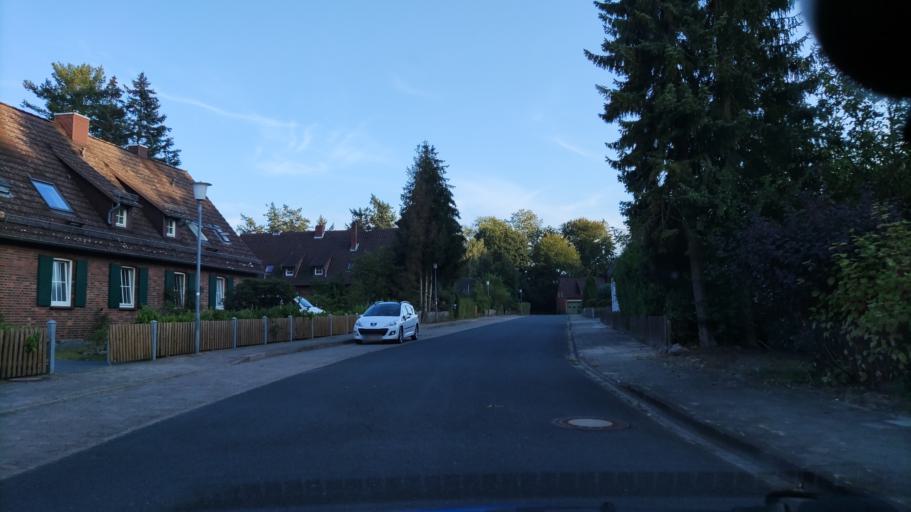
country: DE
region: Lower Saxony
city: Fassberg
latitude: 52.9617
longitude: 10.1855
